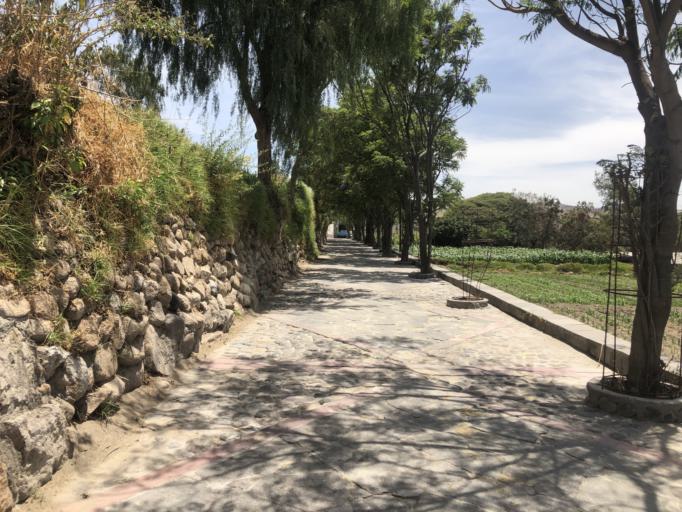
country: PE
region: Arequipa
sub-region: Provincia de Arequipa
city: Quequena
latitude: -16.5557
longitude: -71.4531
